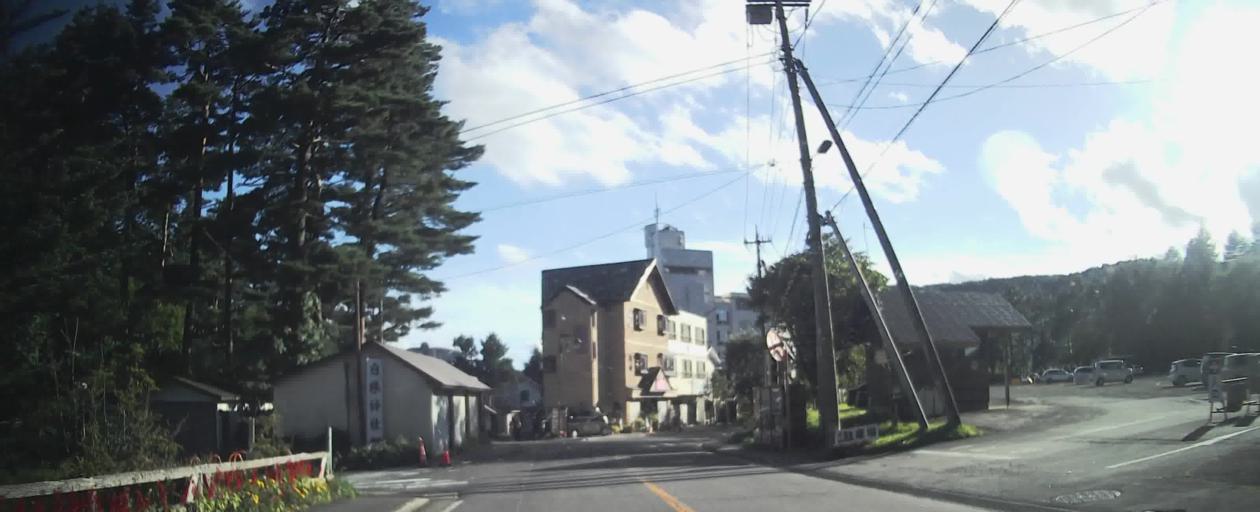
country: JP
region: Gunma
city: Nakanojomachi
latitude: 36.6255
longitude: 138.5952
